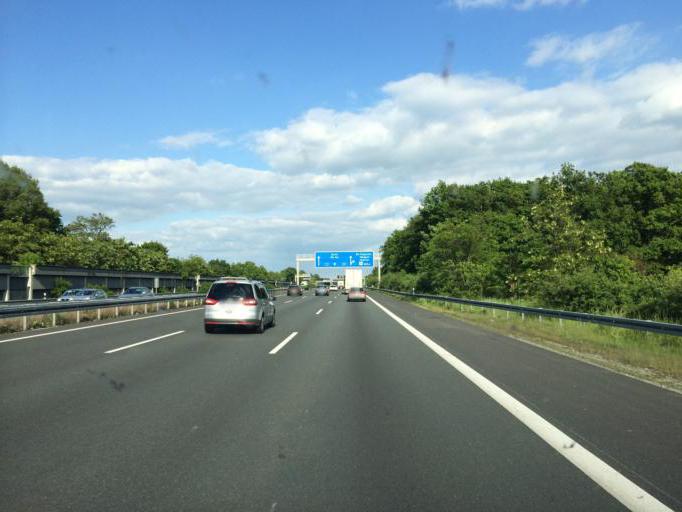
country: DE
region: Lower Saxony
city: Braunschweig
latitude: 52.3131
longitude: 10.5448
